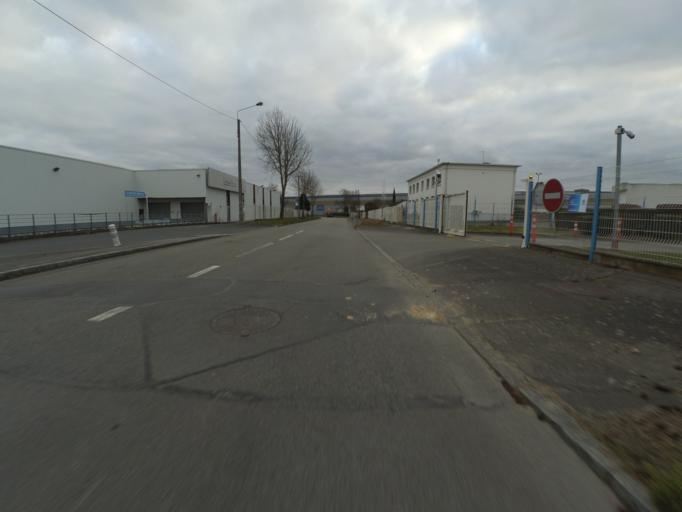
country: FR
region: Pays de la Loire
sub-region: Departement de la Loire-Atlantique
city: Sainte-Luce-sur-Loire
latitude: 47.2654
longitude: -1.4958
